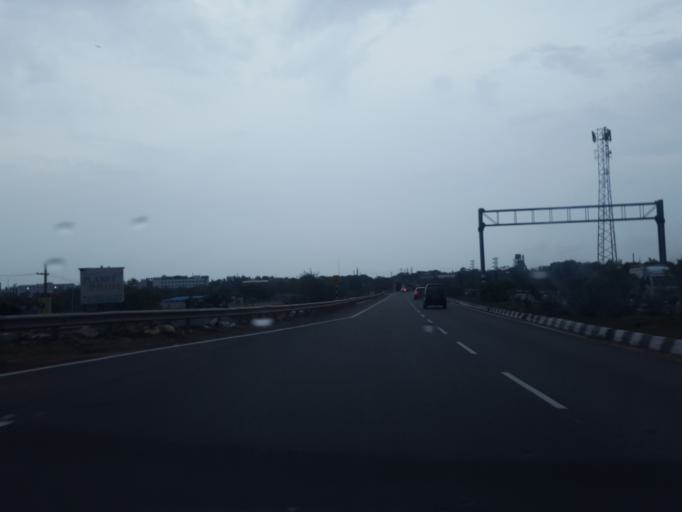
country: IN
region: Telangana
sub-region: Mahbubnagar
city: Farrukhnagar
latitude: 17.1426
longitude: 78.2912
